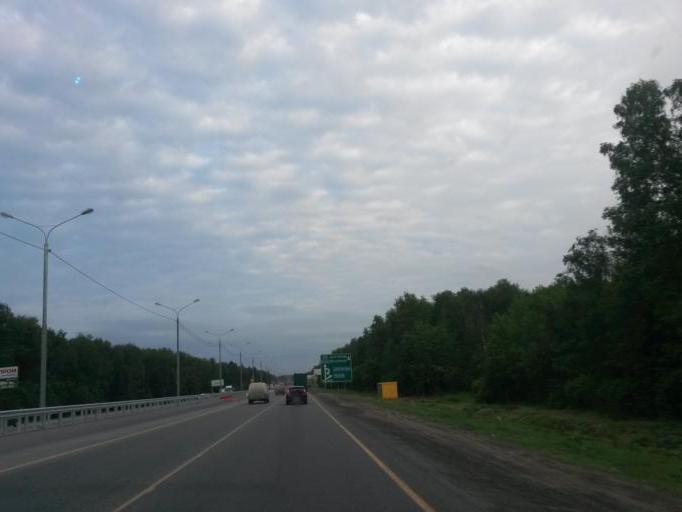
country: RU
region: Moskovskaya
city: Lyubuchany
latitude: 55.2018
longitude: 37.5349
